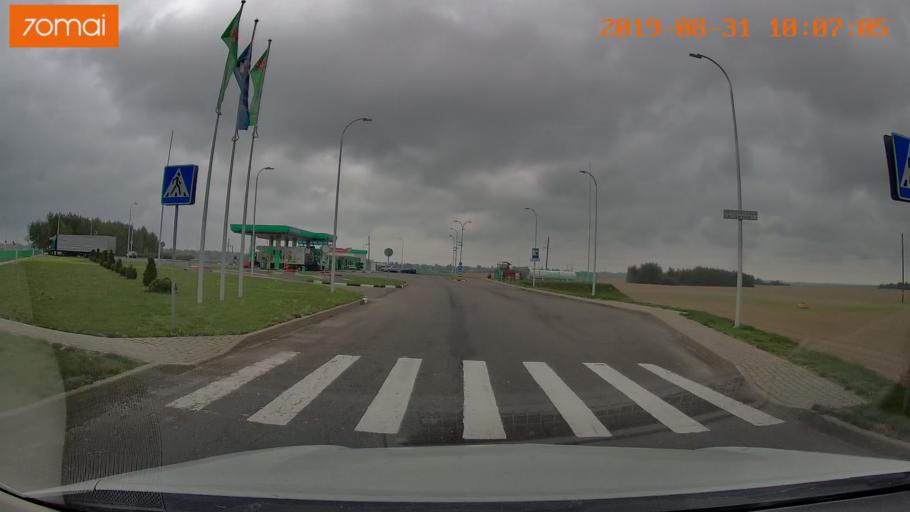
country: BY
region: Mogilev
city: Buynichy
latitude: 53.9532
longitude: 30.2122
